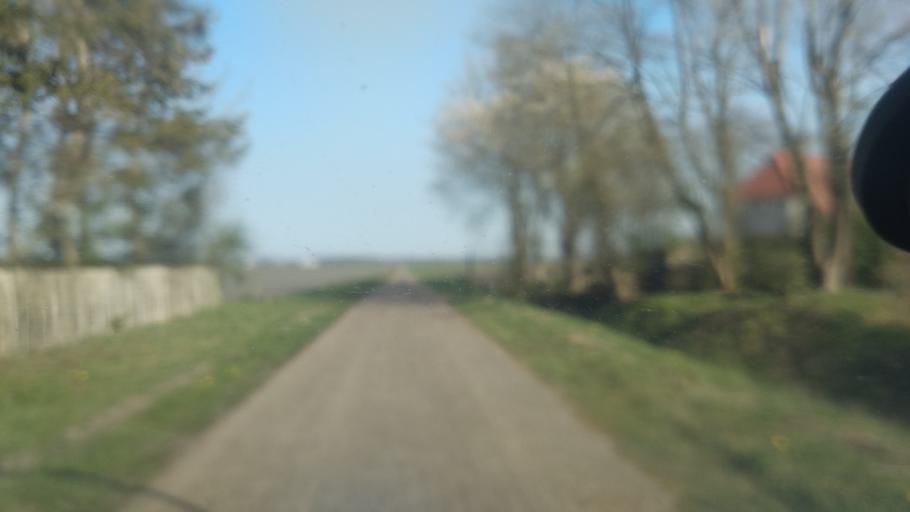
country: NL
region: Drenthe
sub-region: Gemeente Borger-Odoorn
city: Borger
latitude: 52.8904
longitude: 6.7909
